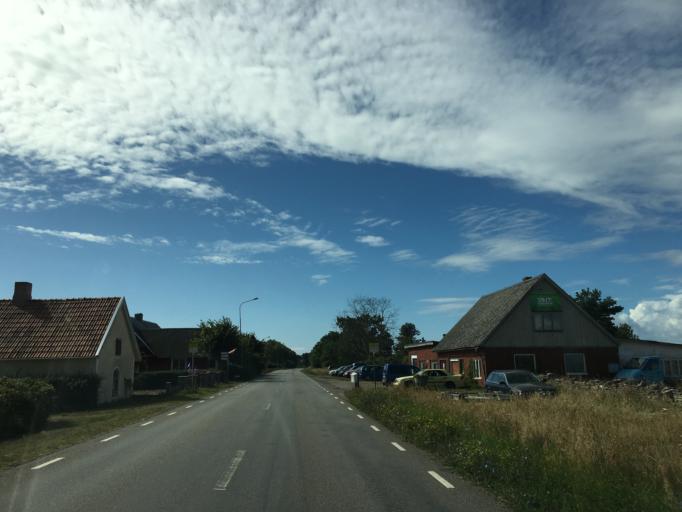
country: SE
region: Kalmar
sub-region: Morbylanga Kommun
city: Moerbylanga
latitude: 56.4495
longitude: 16.4286
